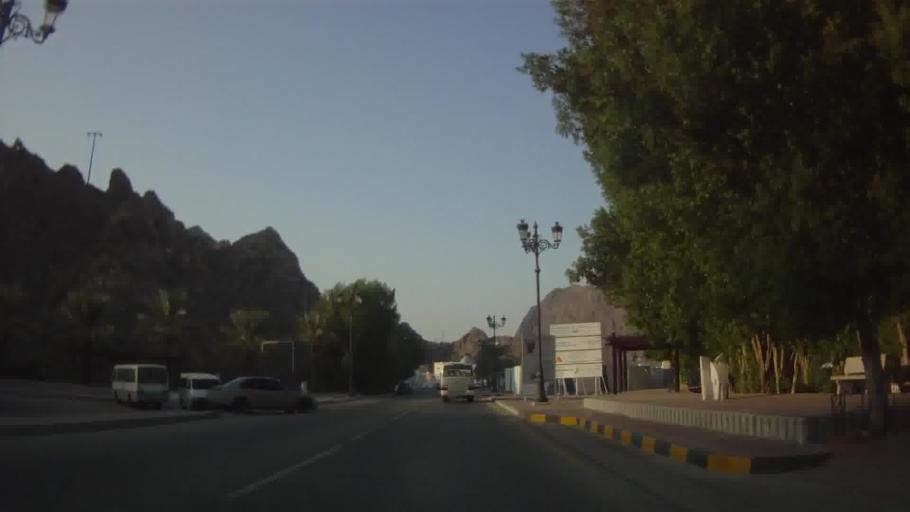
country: OM
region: Muhafazat Masqat
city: Muscat
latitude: 23.5976
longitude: 58.5973
